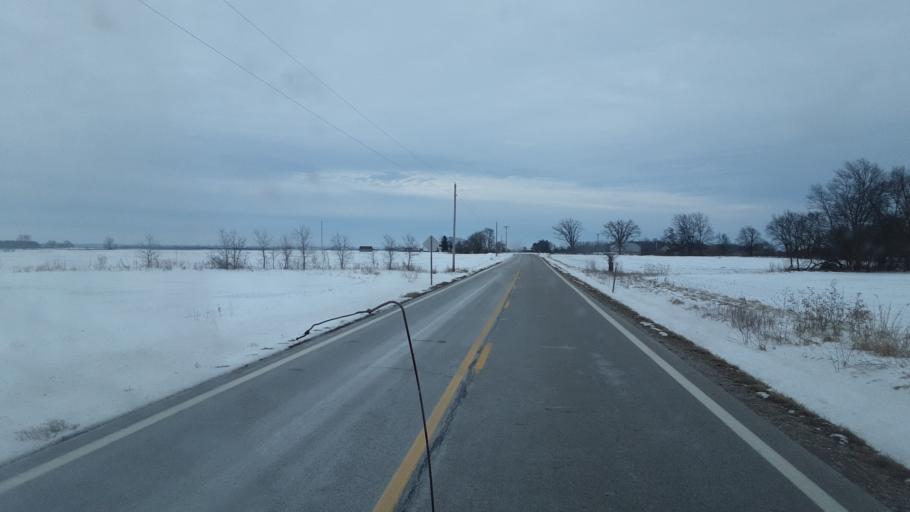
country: US
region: Ohio
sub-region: Pickaway County
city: Williamsport
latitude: 39.6371
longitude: -83.0777
